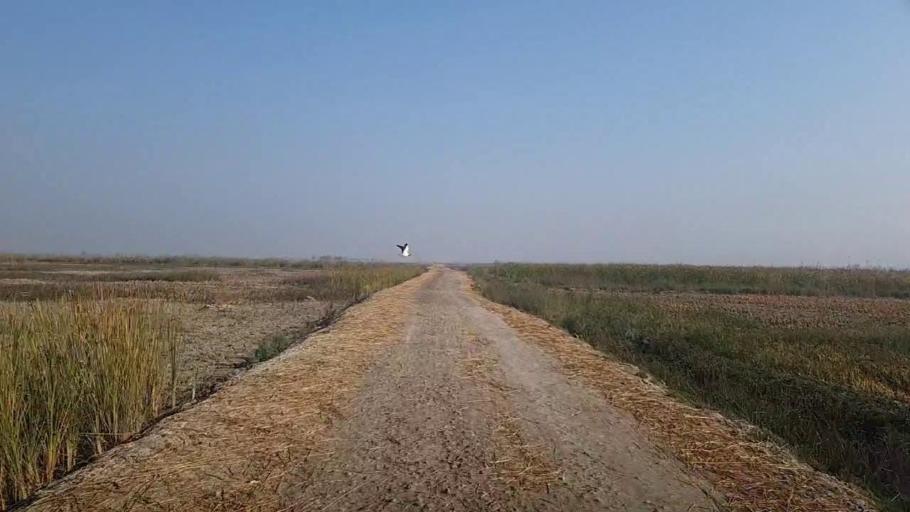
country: PK
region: Sindh
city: Radhan
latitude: 27.1311
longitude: 67.9027
